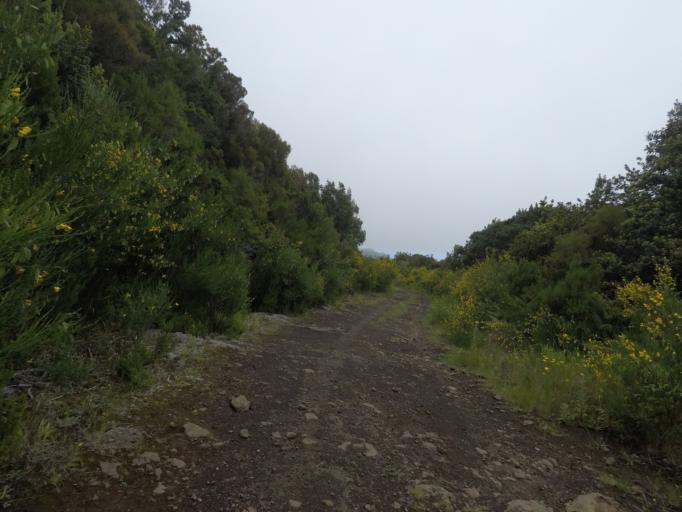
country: PT
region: Madeira
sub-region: Sao Vicente
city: Sao Vicente
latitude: 32.7713
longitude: -17.0563
